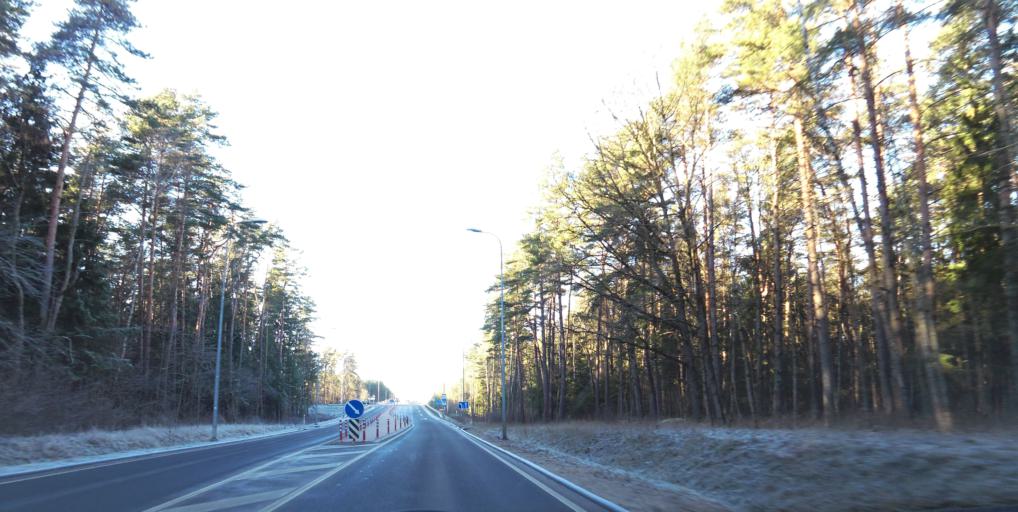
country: LT
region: Vilnius County
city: Lazdynai
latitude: 54.6441
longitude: 25.1555
